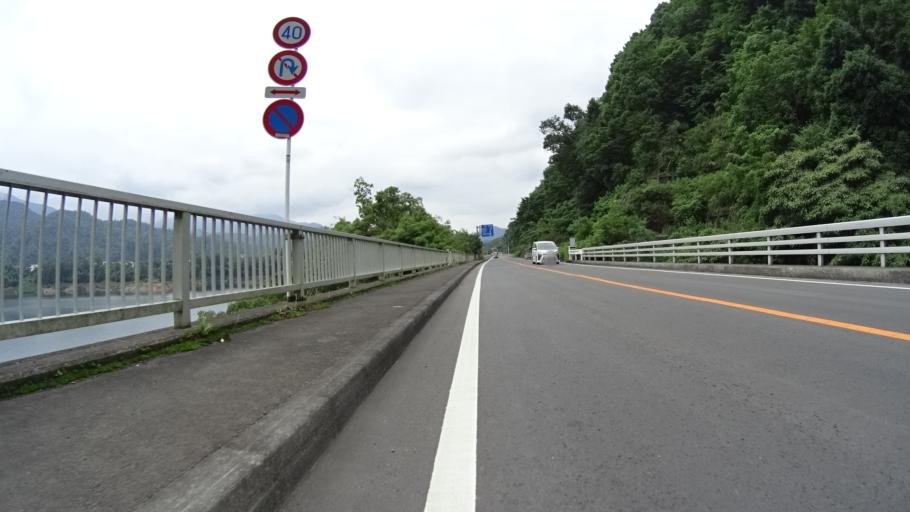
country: JP
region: Kanagawa
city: Atsugi
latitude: 35.5222
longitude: 139.2392
